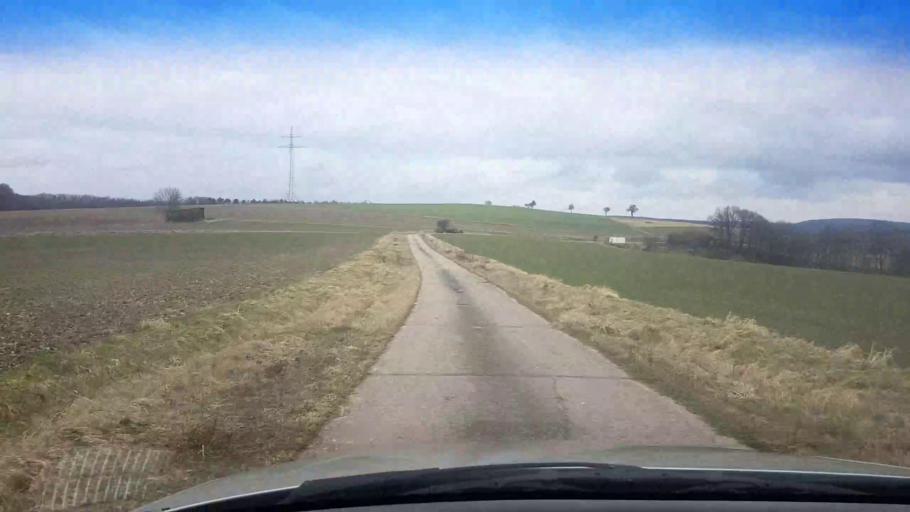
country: DE
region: Bavaria
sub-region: Regierungsbezirk Unterfranken
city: Stettfeld
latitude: 49.9407
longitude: 10.7141
